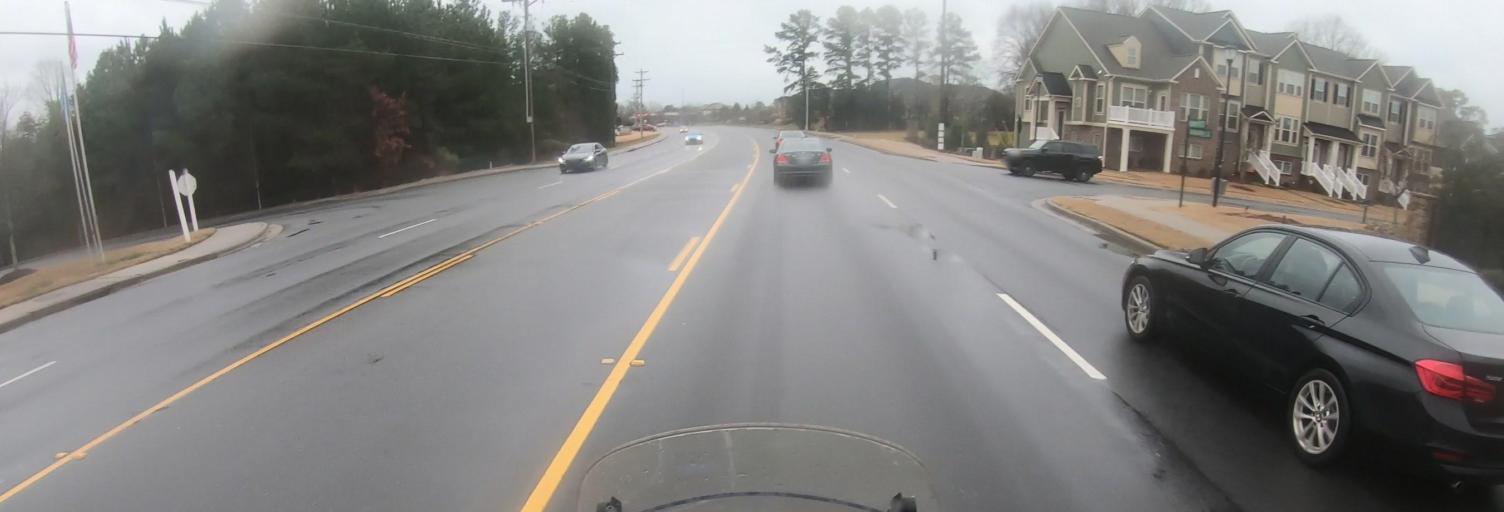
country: US
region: South Carolina
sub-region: York County
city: Tega Cay
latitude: 35.0516
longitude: -80.9920
